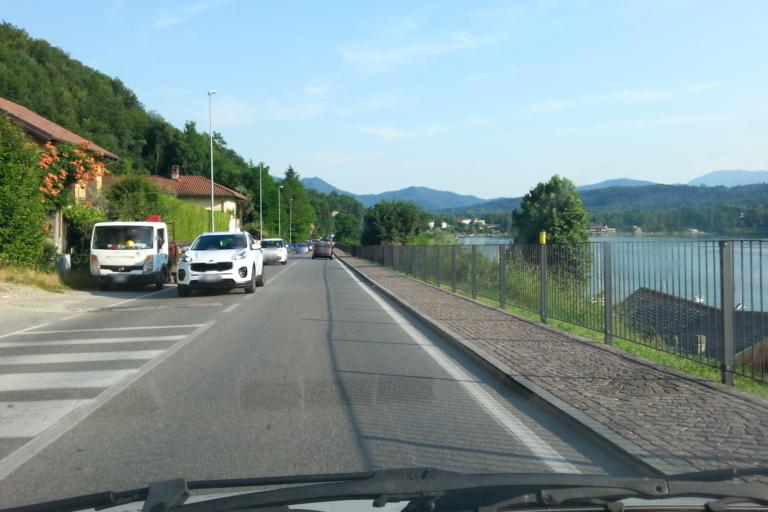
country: IT
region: Piedmont
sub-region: Provincia di Torino
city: Avigliana
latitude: 45.0696
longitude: 7.3921
